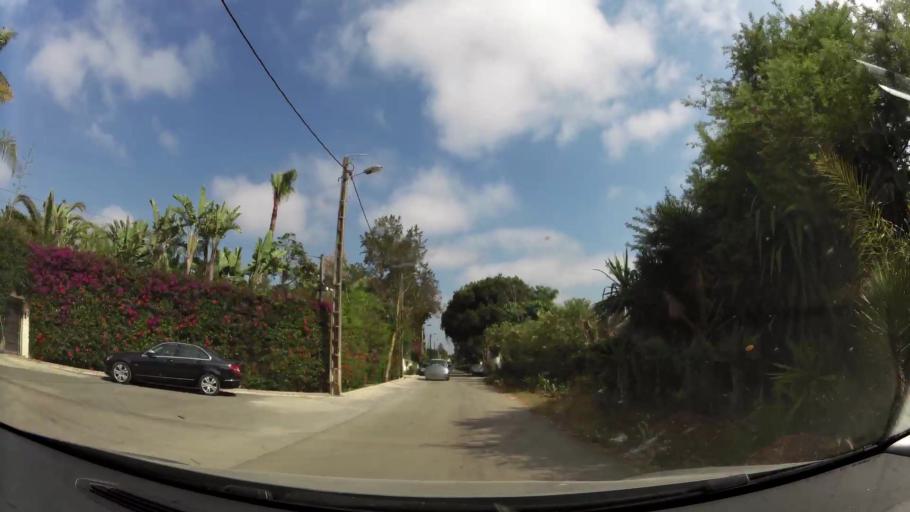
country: MA
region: Rabat-Sale-Zemmour-Zaer
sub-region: Rabat
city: Rabat
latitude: 33.9841
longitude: -6.8395
